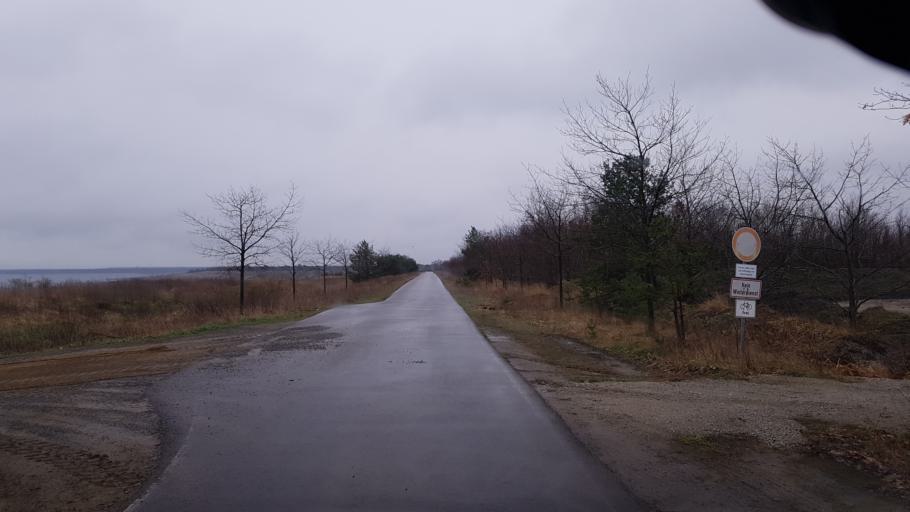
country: DE
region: Brandenburg
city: Grossraschen
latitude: 51.5747
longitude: 13.9833
